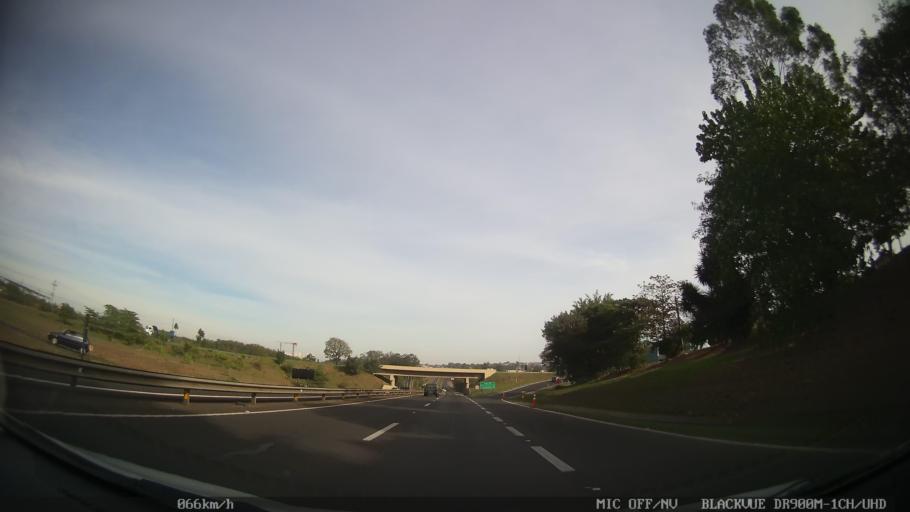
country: BR
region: Sao Paulo
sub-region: Piracicaba
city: Piracicaba
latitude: -22.6831
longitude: -47.6867
